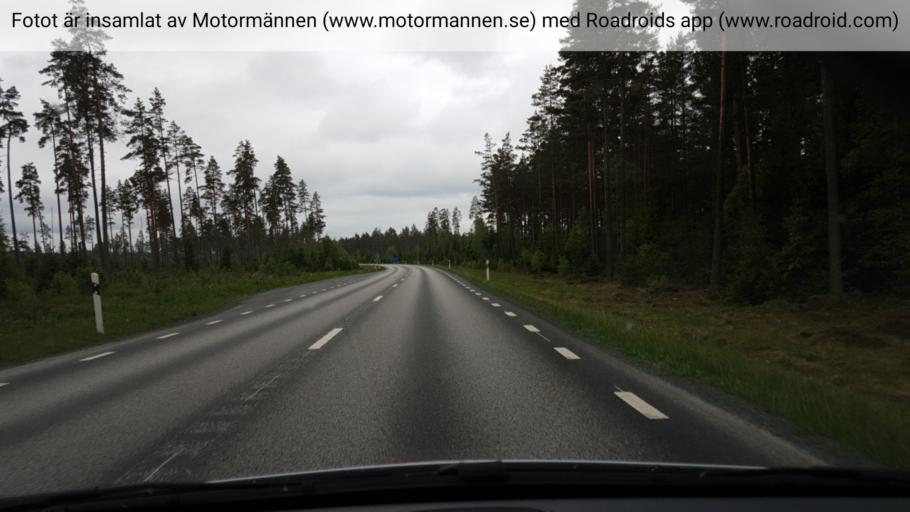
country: SE
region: Joenkoeping
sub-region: Mullsjo Kommun
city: Mullsjoe
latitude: 57.7044
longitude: 13.8483
